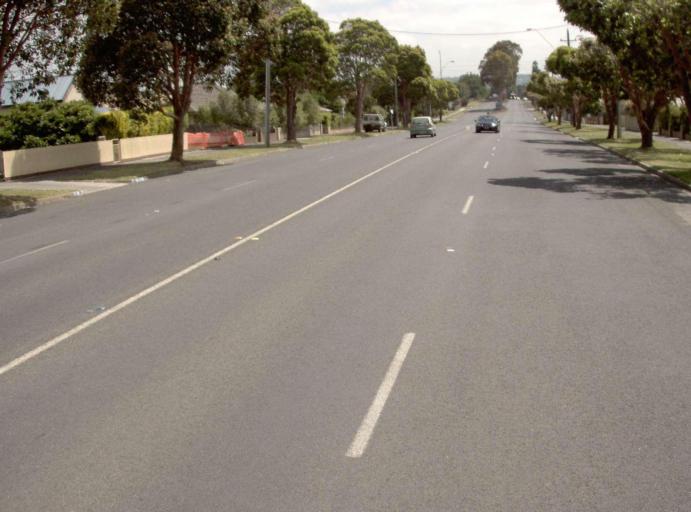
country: AU
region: Victoria
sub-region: Baw Baw
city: Warragul
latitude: -38.4739
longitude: 145.9484
